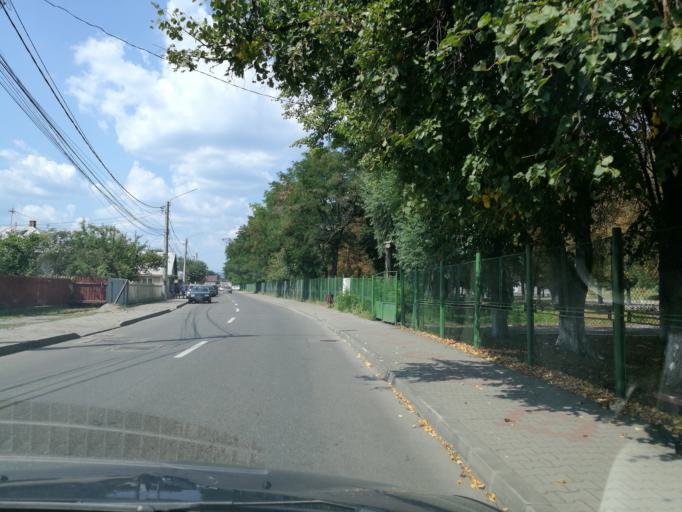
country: RO
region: Neamt
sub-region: Oras Targu Neamt
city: Humulesti
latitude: 47.2094
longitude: 26.3473
